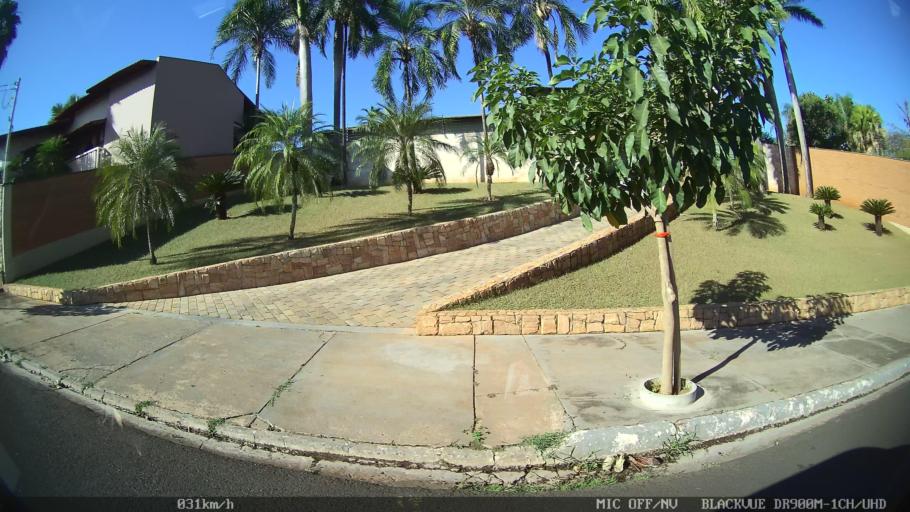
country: BR
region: Sao Paulo
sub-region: Olimpia
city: Olimpia
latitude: -20.7430
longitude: -48.9025
